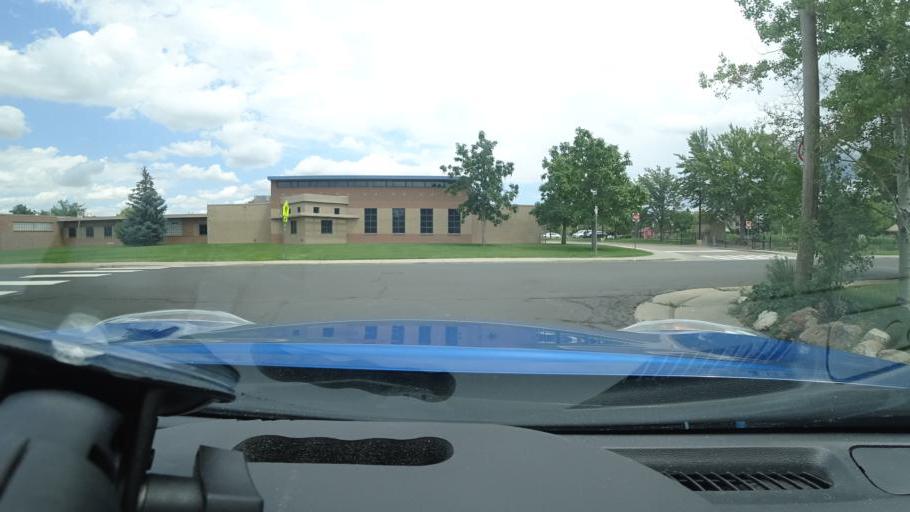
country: US
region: Colorado
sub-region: Adams County
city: Aurora
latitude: 39.7242
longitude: -104.8314
